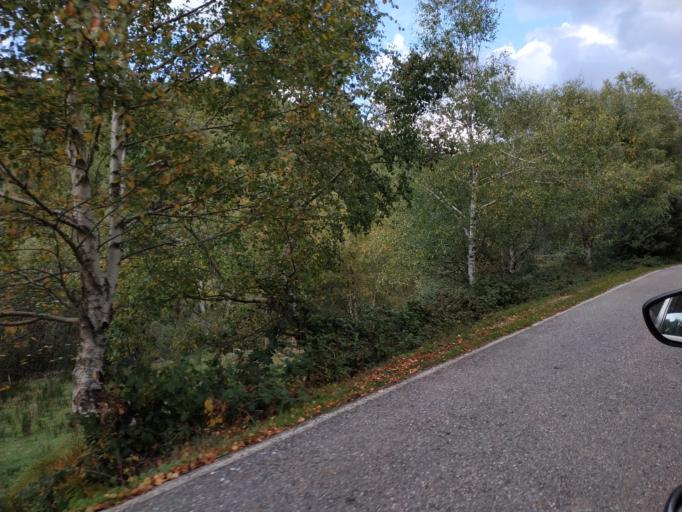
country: ES
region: Castille and Leon
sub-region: Provincia de Leon
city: Candin
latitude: 42.8663
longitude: -6.8427
